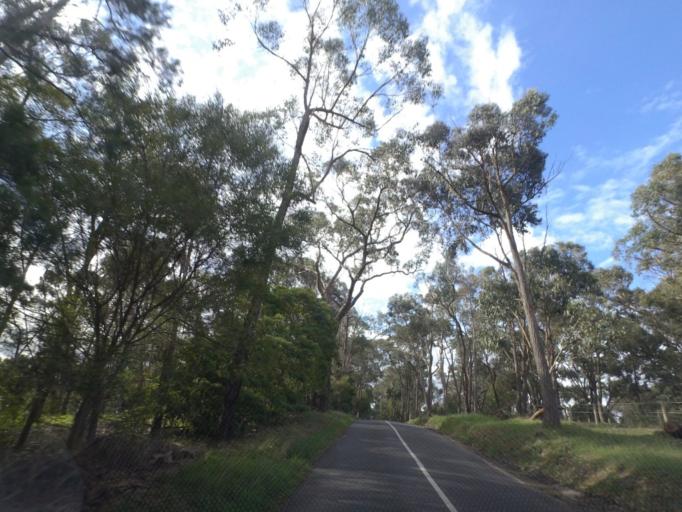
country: AU
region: Victoria
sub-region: Yarra Ranges
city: Mount Evelyn
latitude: -37.7552
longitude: 145.4103
